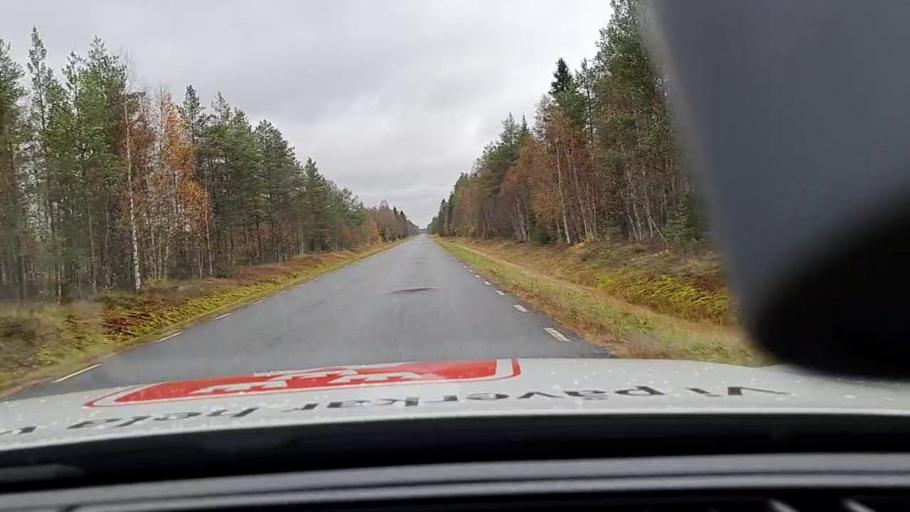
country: SE
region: Norrbotten
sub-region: Haparanda Kommun
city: Haparanda
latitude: 65.9113
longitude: 23.8291
